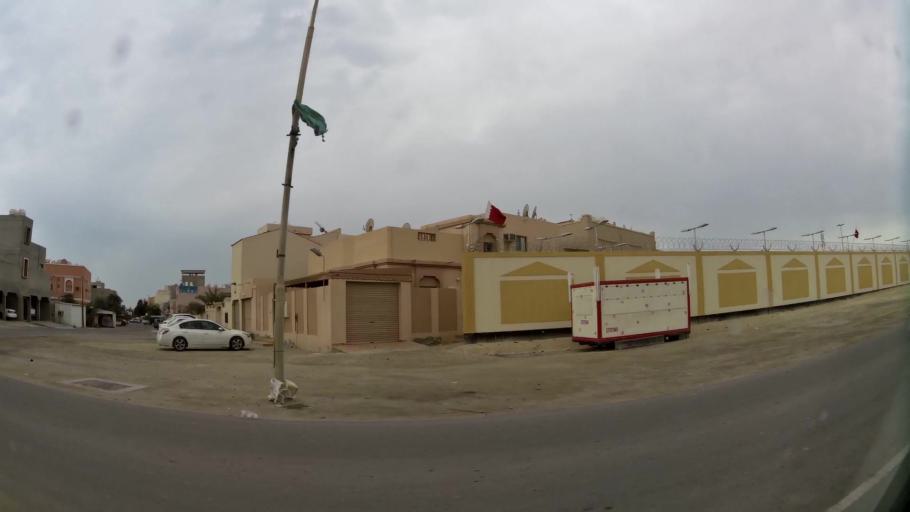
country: BH
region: Central Governorate
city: Madinat Hamad
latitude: 26.1297
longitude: 50.4787
